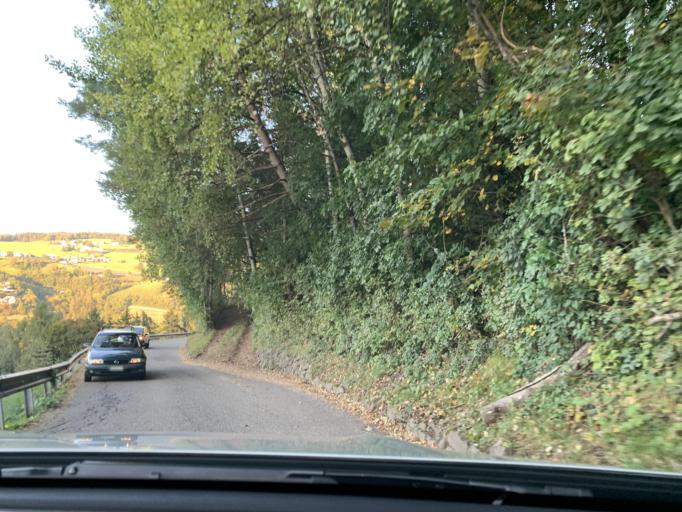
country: IT
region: Trentino-Alto Adige
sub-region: Bolzano
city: Fie Allo Sciliar
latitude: 46.5057
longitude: 11.5002
